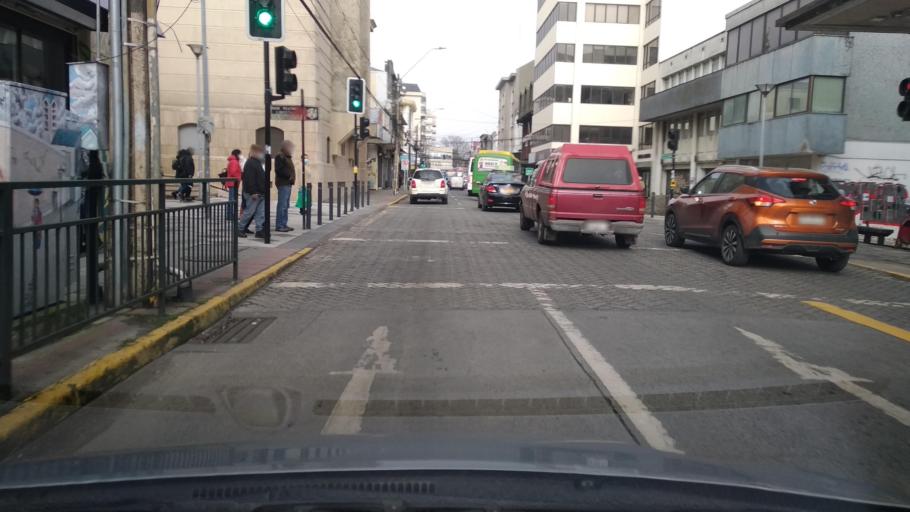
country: CL
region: Los Rios
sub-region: Provincia de Valdivia
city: Valdivia
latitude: -39.8134
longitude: -73.2465
